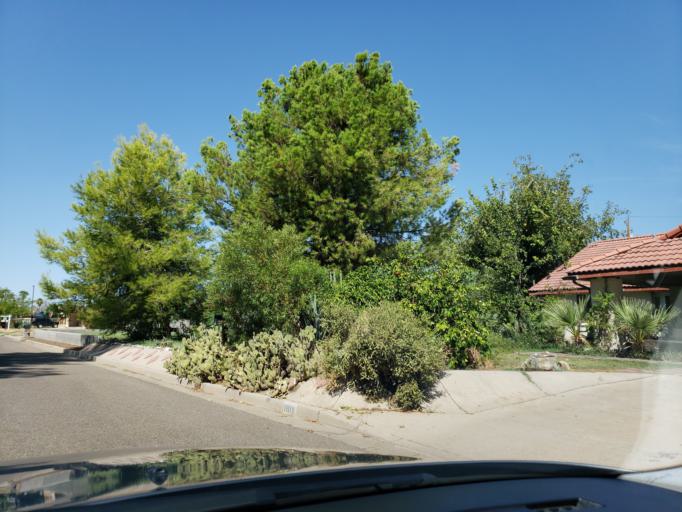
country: US
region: Arizona
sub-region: Maricopa County
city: Glendale
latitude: 33.5571
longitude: -112.0979
